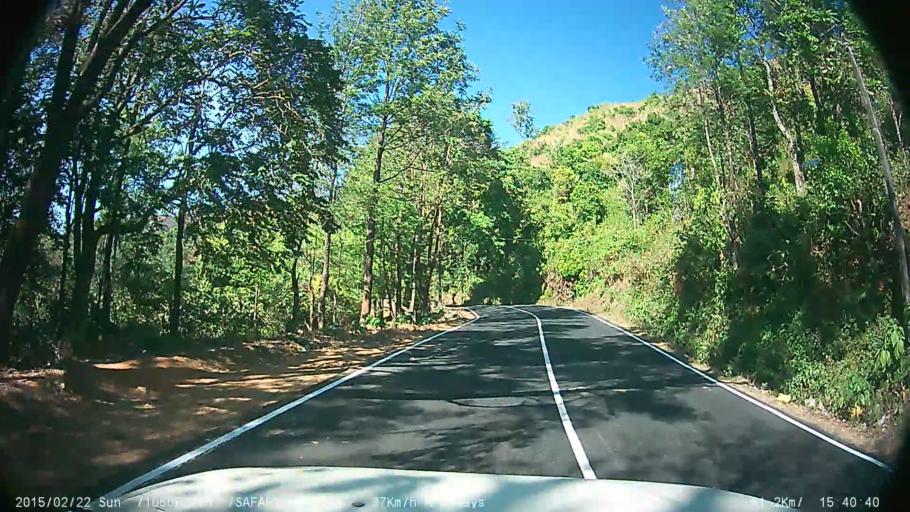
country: IN
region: Kerala
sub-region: Kottayam
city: Erattupetta
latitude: 9.5708
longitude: 76.9749
